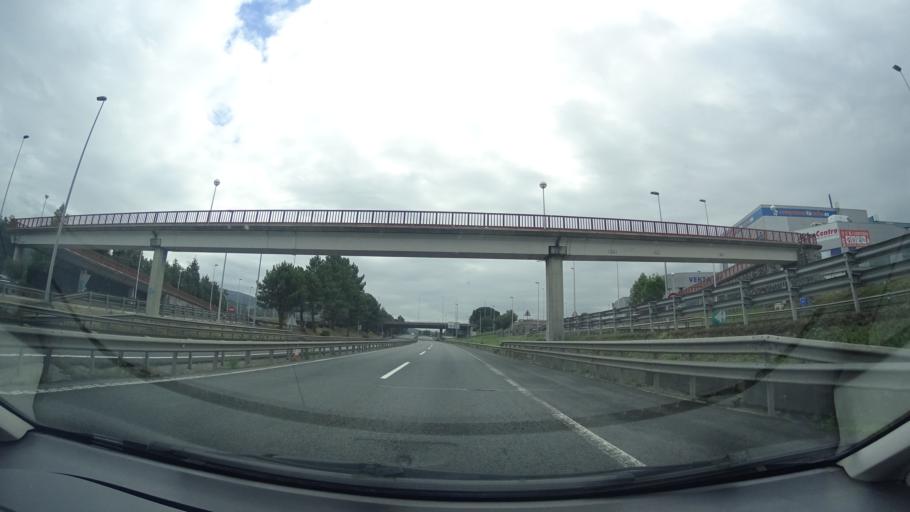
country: ES
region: Basque Country
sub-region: Bizkaia
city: Basauri
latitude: 43.2311
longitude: -2.8815
